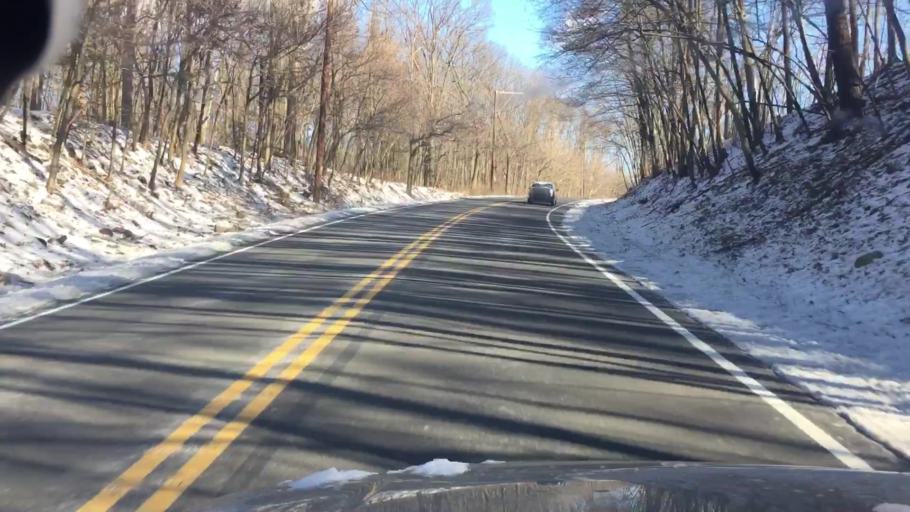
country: US
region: Pennsylvania
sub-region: Luzerne County
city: Nescopeck
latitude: 41.0556
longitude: -76.1834
